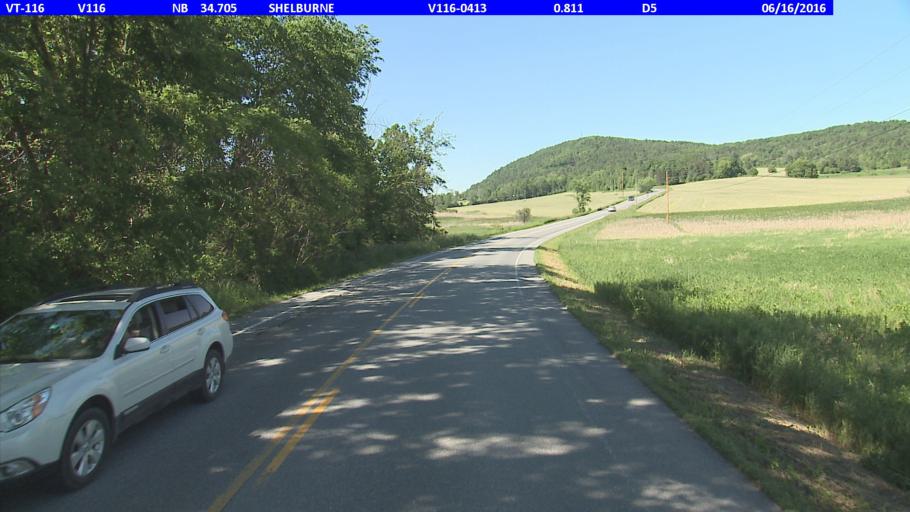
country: US
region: Vermont
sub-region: Chittenden County
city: Hinesburg
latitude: 44.3906
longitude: -73.1423
